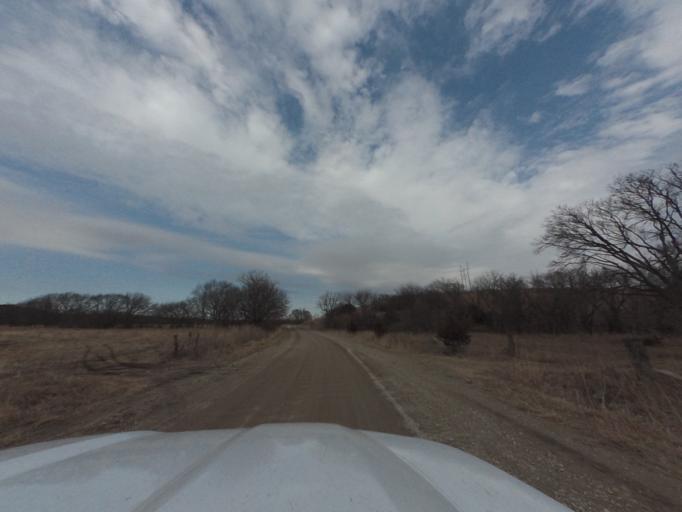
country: US
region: Kansas
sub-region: Chase County
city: Cottonwood Falls
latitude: 38.2784
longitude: -96.7337
